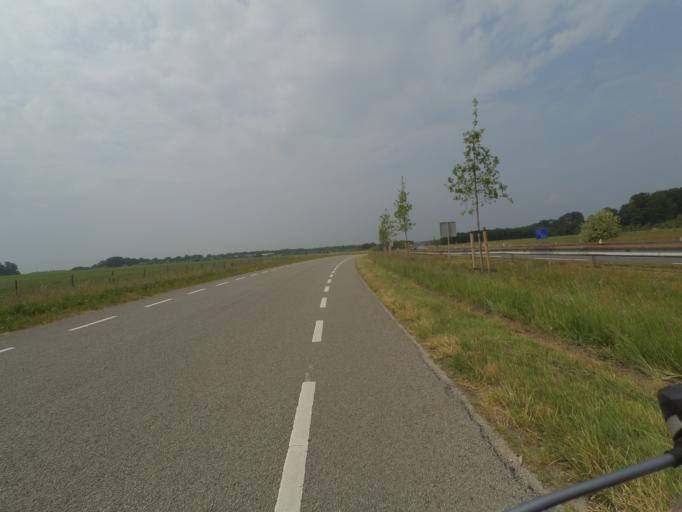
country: NL
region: Gelderland
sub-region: Gemeente Renkum
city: Heelsum
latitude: 51.9749
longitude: 5.7721
